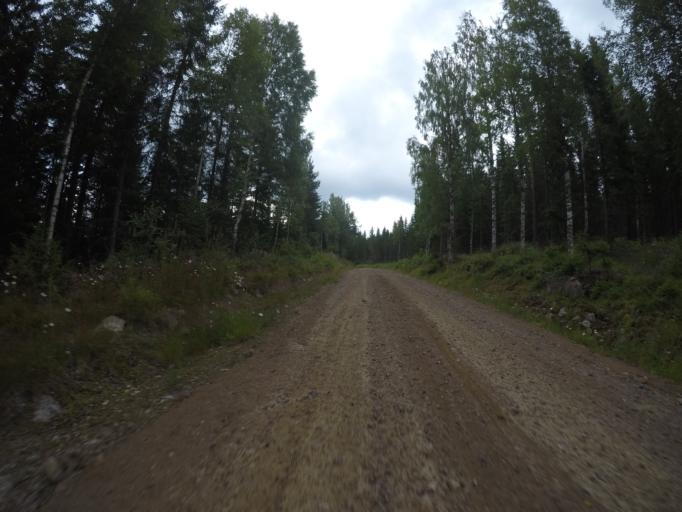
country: SE
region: Vaermland
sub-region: Filipstads Kommun
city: Lesjofors
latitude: 60.1980
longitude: 14.3585
